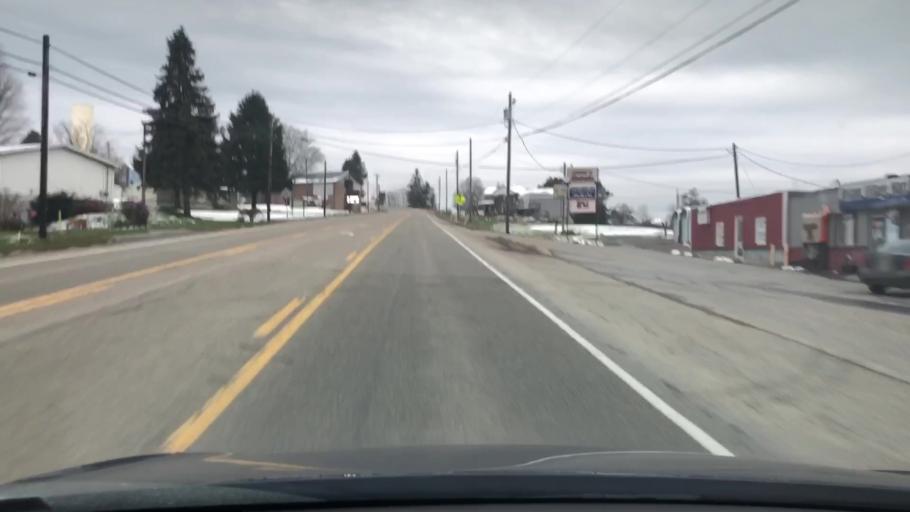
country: US
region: Pennsylvania
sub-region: Armstrong County
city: Kittanning
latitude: 40.9748
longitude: -79.3481
